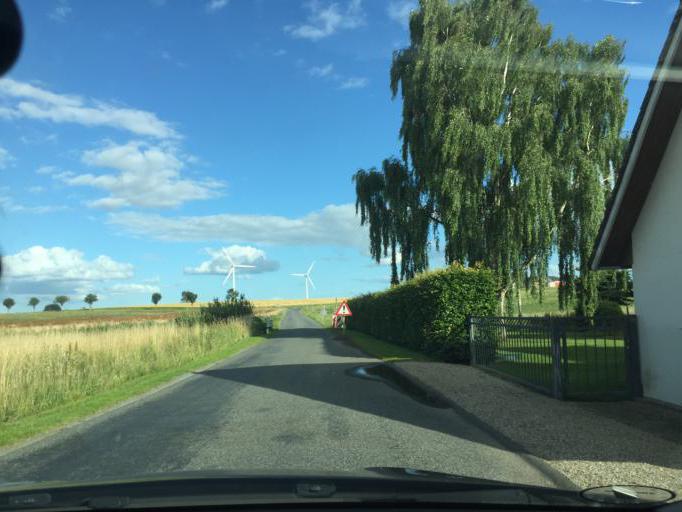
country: DK
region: South Denmark
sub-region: Faaborg-Midtfyn Kommune
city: Arslev
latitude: 55.2949
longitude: 10.5366
